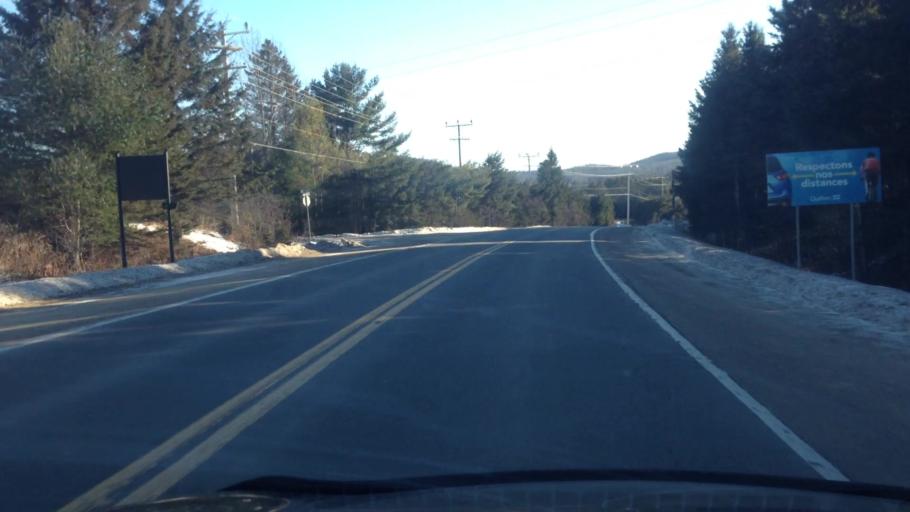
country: CA
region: Quebec
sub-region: Laurentides
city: Mont-Tremblant
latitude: 46.0494
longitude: -74.6093
